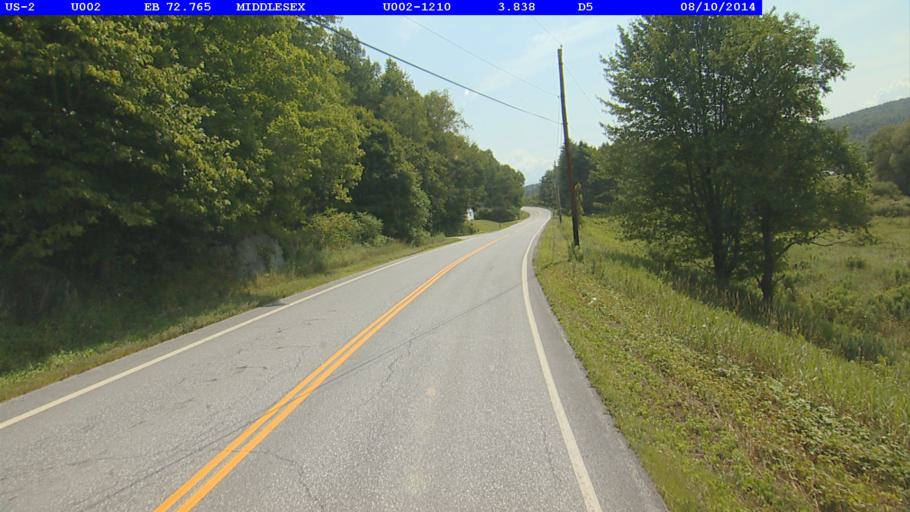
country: US
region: Vermont
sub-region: Washington County
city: Montpelier
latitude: 44.2751
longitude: -72.6405
